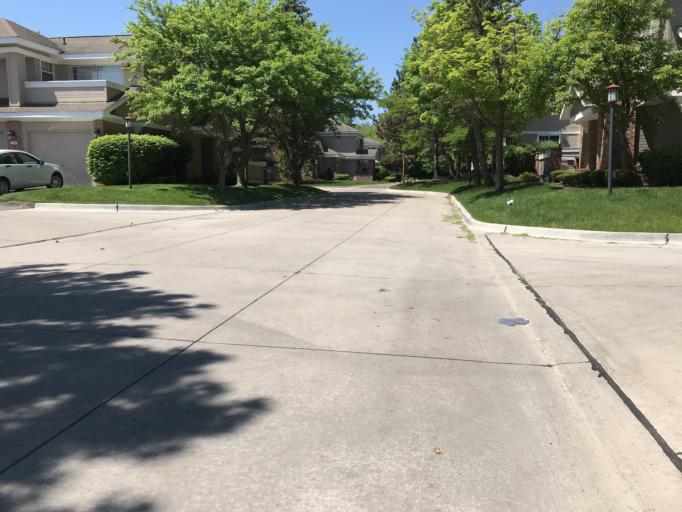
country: US
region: Michigan
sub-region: Oakland County
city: West Bloomfield Township
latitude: 42.5409
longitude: -83.3666
